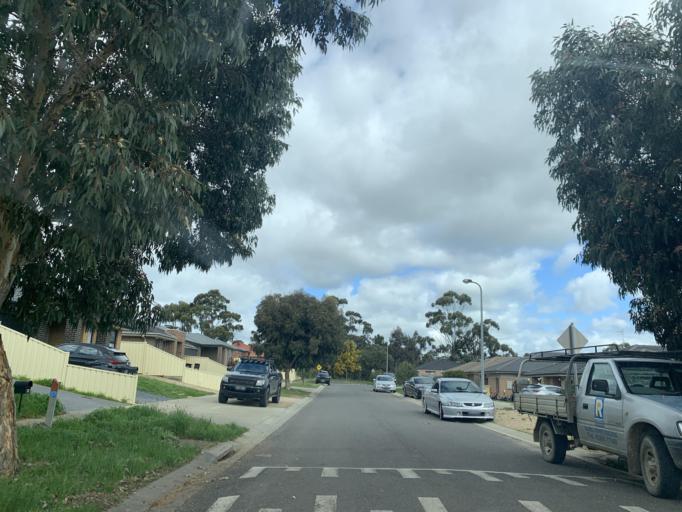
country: AU
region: Victoria
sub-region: Whittlesea
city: Whittlesea
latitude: -37.2925
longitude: 144.9312
